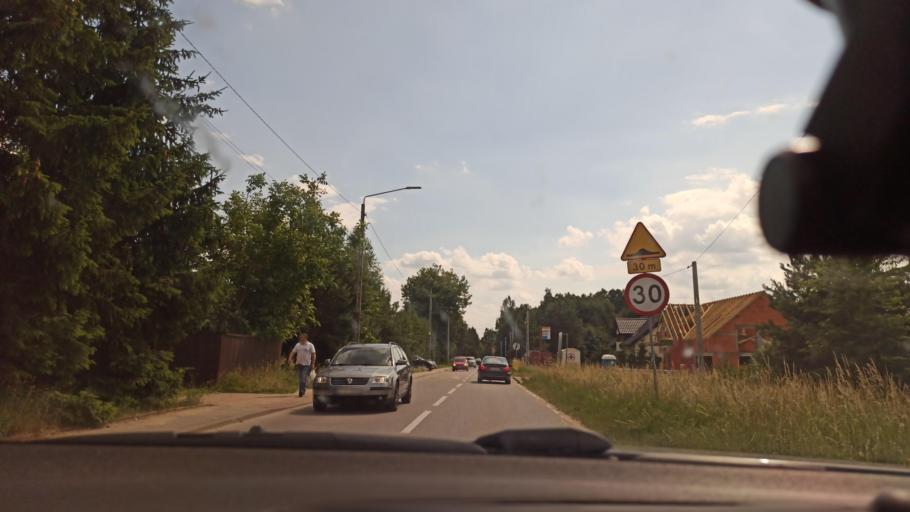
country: PL
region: Podlasie
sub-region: Powiat bialostocki
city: Turosn Koscielna
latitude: 53.0688
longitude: 23.1009
